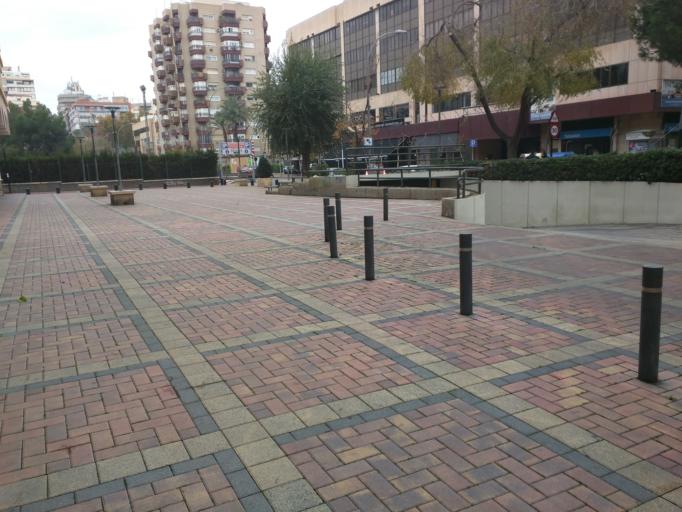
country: ES
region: Murcia
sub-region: Murcia
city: Murcia
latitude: 37.9896
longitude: -1.1275
